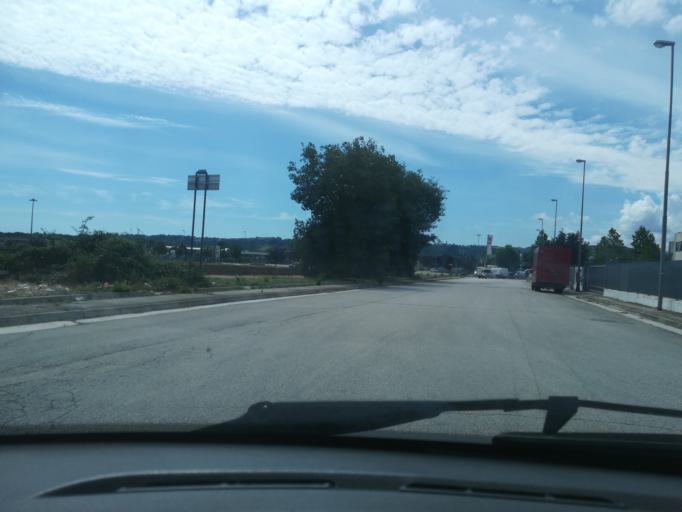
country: IT
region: The Marches
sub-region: Provincia di Macerata
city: Santa Maria Apparente
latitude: 43.2843
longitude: 13.6810
